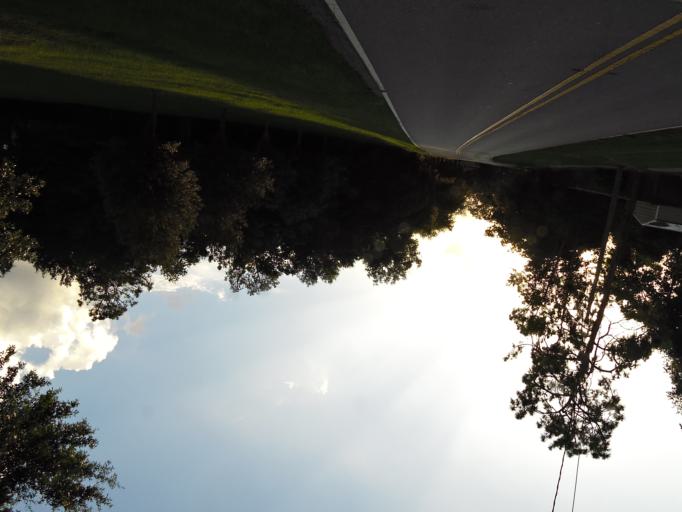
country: US
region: Florida
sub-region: Saint Johns County
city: Fruit Cove
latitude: 30.1382
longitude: -81.6353
